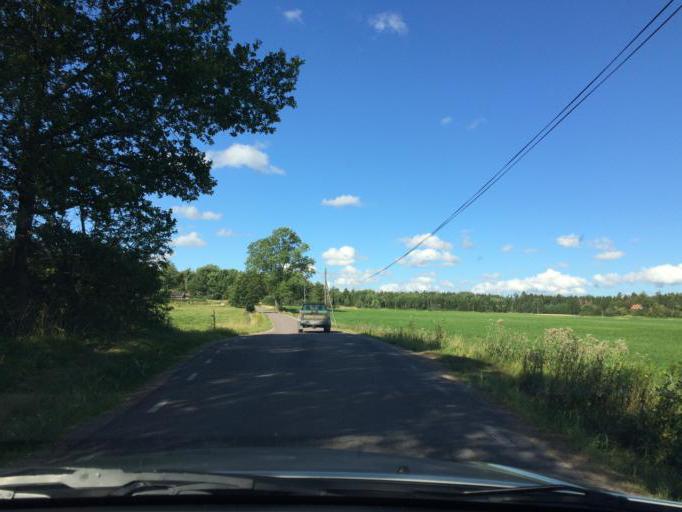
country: SE
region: Soedermanland
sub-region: Eskilstuna Kommun
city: Kvicksund
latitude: 59.4953
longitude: 16.3376
